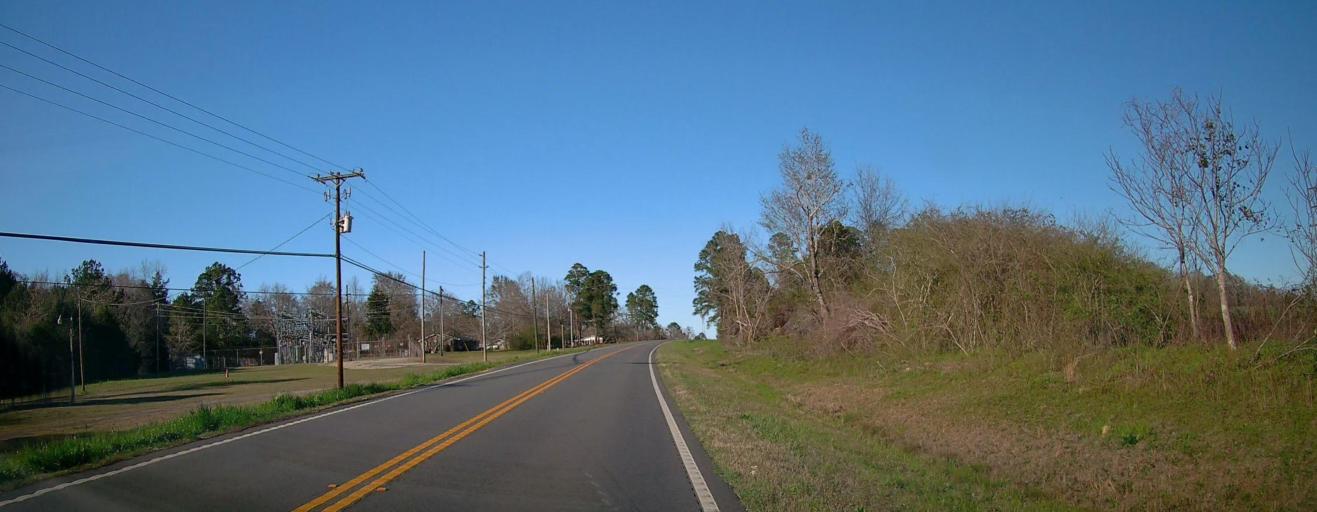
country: US
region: Georgia
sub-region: Taylor County
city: Reynolds
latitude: 32.5458
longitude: -84.1004
